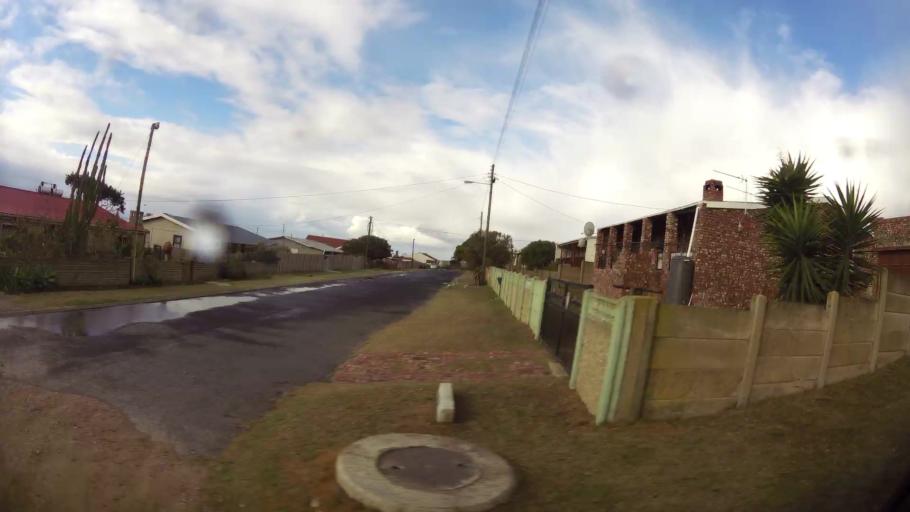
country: ZA
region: Western Cape
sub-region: Eden District Municipality
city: Mossel Bay
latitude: -34.1873
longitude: 22.1215
